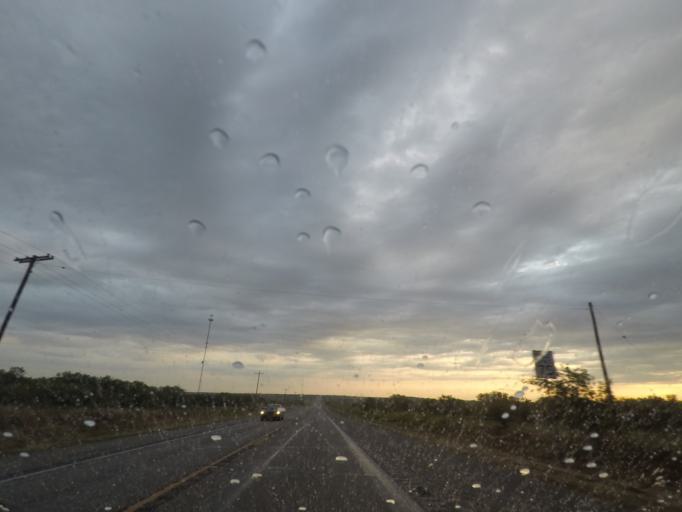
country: US
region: Texas
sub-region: Clay County
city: Henrietta
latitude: 34.0214
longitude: -98.2237
